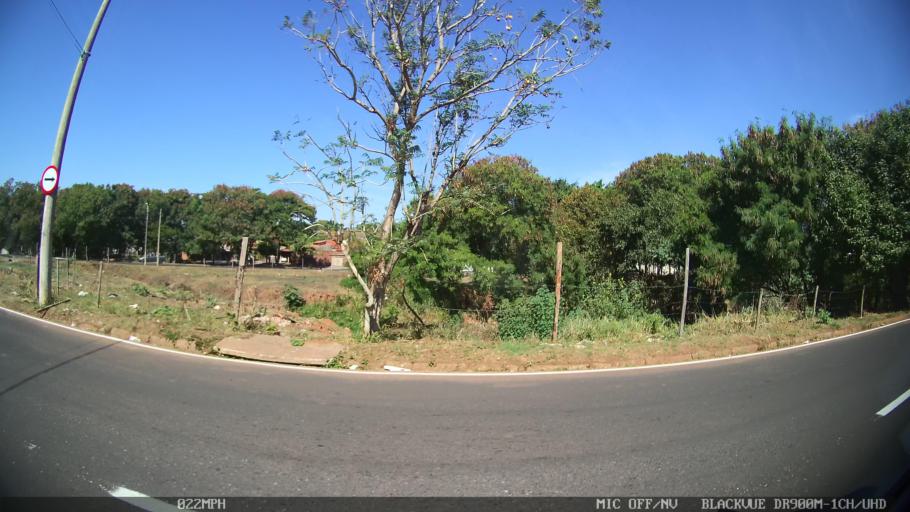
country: BR
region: Sao Paulo
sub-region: Sao Jose Do Rio Preto
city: Sao Jose do Rio Preto
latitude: -20.7727
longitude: -49.4033
